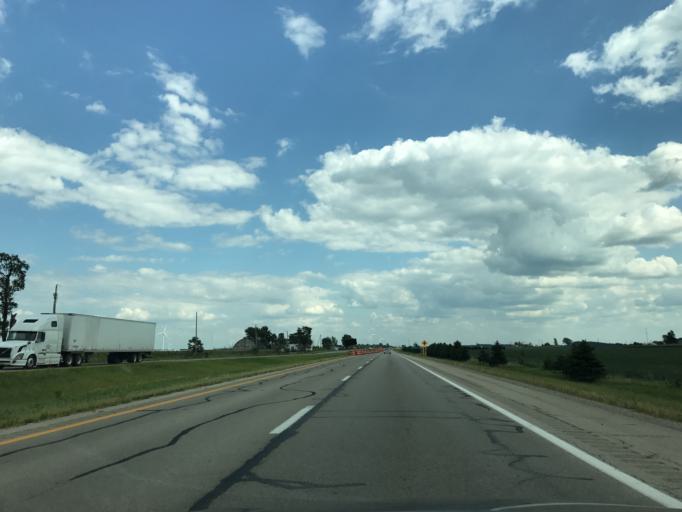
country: US
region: Ohio
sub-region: Van Wert County
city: Convoy
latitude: 40.9564
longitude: -84.7319
